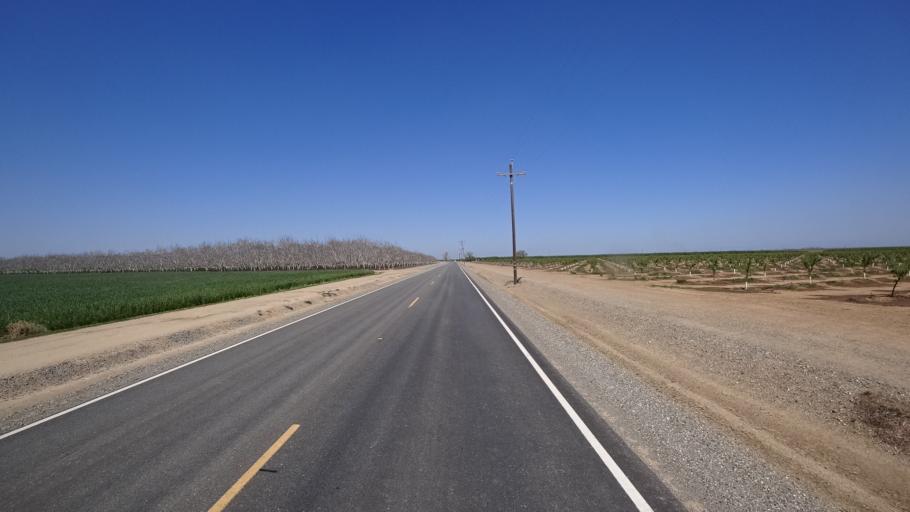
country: US
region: California
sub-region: Glenn County
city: Willows
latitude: 39.6075
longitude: -122.1377
